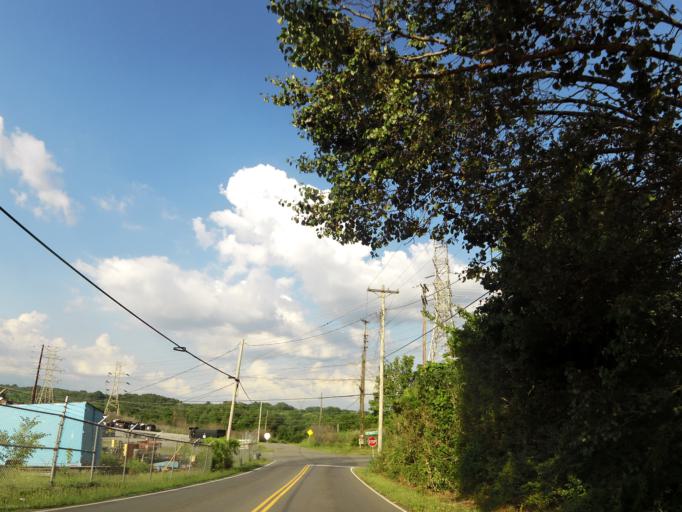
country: US
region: Tennessee
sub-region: Montgomery County
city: Clarksville
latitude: 36.5349
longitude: -87.3377
